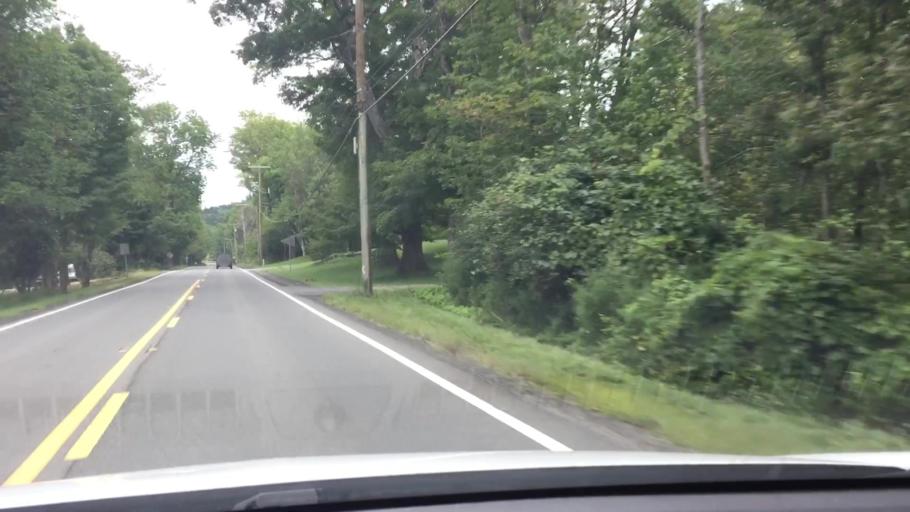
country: US
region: Massachusetts
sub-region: Berkshire County
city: Hinsdale
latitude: 42.3958
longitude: -73.1246
